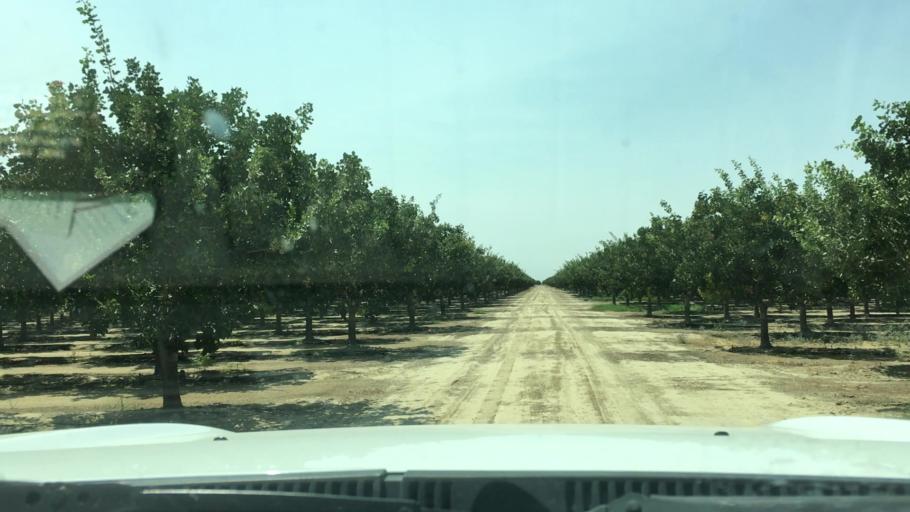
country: US
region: California
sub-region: Tulare County
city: Earlimart
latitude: 35.8256
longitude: -119.3619
